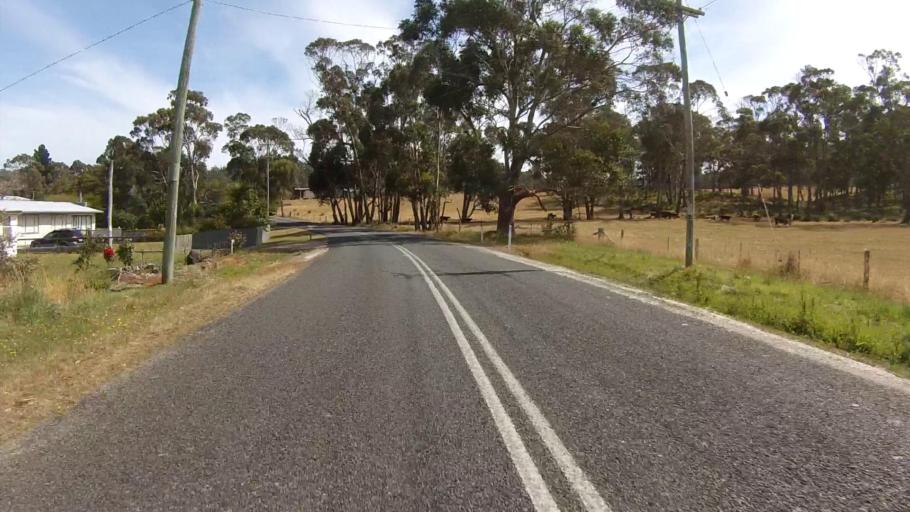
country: AU
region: Tasmania
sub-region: Huon Valley
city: Cygnet
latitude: -43.2762
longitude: 147.1623
